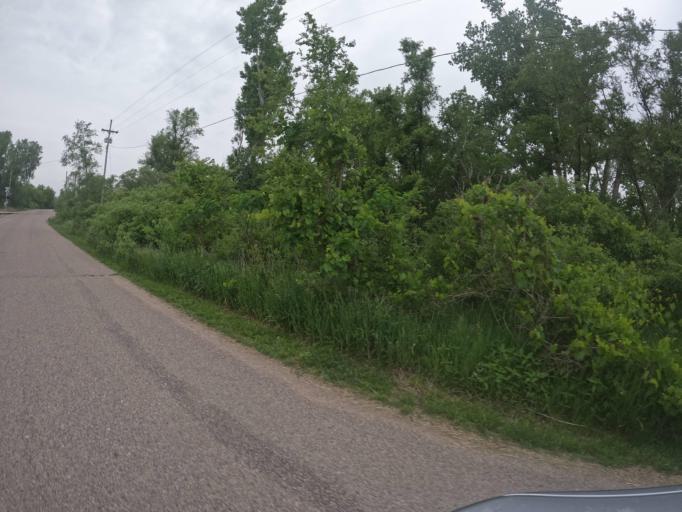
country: US
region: Nebraska
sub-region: Sarpy County
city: Offutt Air Force Base
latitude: 41.0523
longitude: -95.9519
